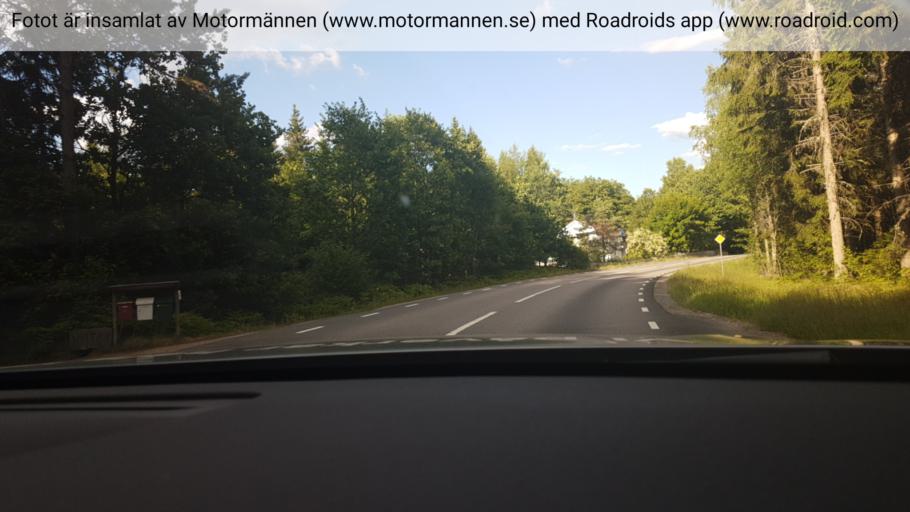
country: SE
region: Vaestra Goetaland
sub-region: Tranemo Kommun
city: Limmared
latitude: 57.5707
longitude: 13.5493
